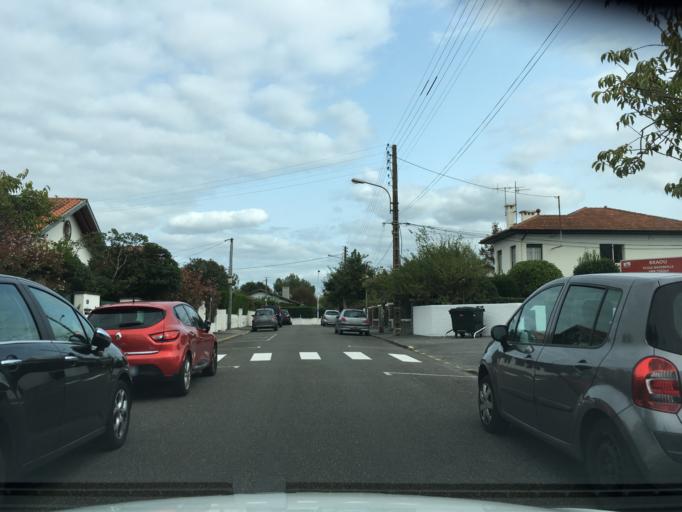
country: FR
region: Aquitaine
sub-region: Departement des Pyrenees-Atlantiques
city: Biarritz
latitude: 43.4748
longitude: -1.5418
